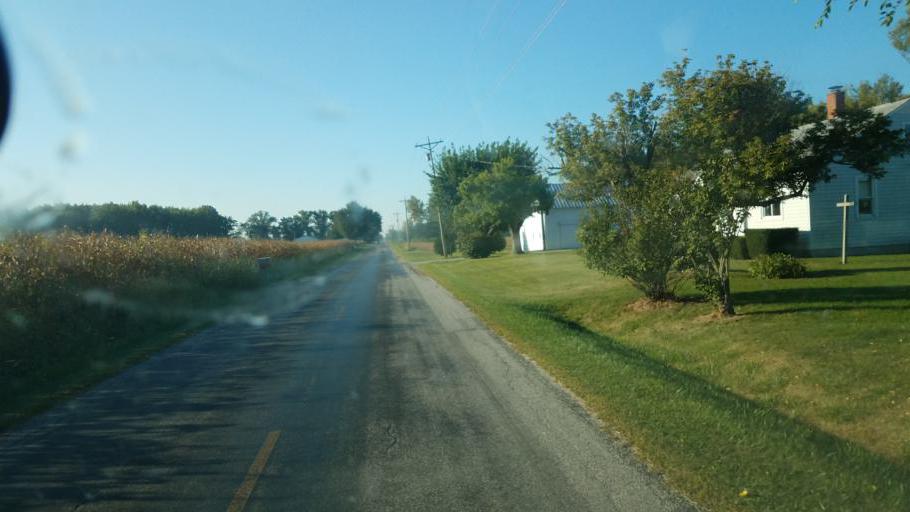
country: US
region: Ohio
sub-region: Morrow County
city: Cardington
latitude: 40.5520
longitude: -82.9957
